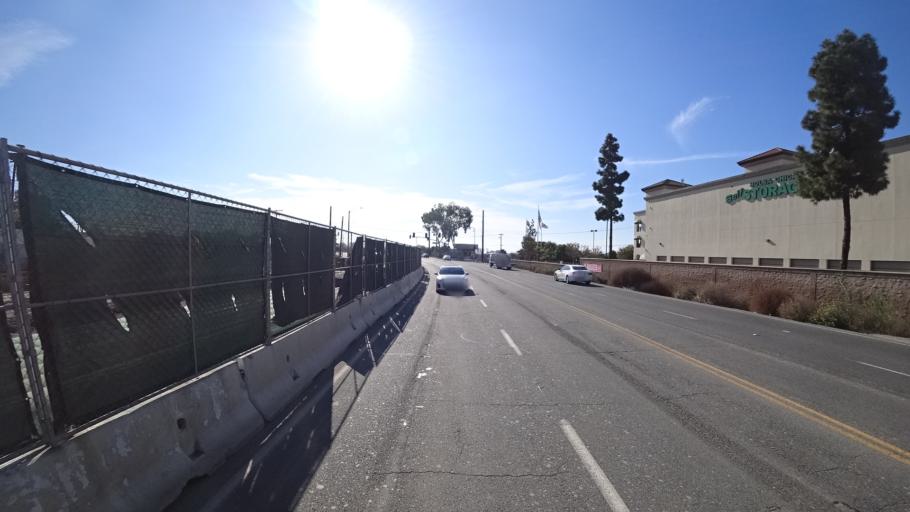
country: US
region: California
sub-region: Orange County
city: Westminster
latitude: 33.7714
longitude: -118.0415
